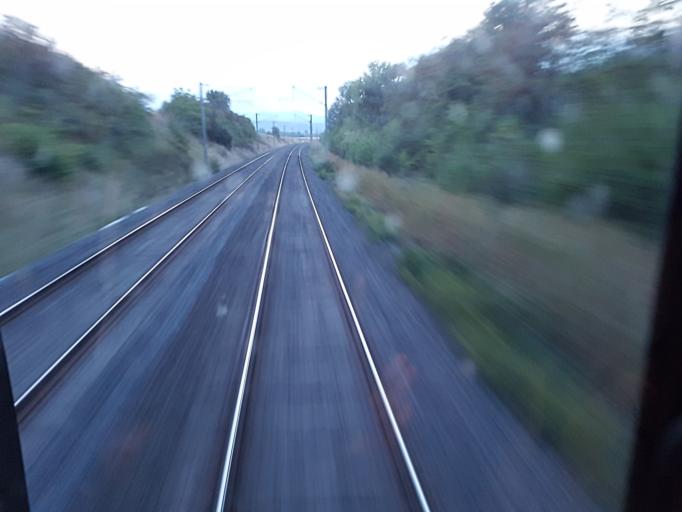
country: FR
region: Auvergne
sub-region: Departement du Puy-de-Dome
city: Ennezat
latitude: 45.9121
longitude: 3.2102
